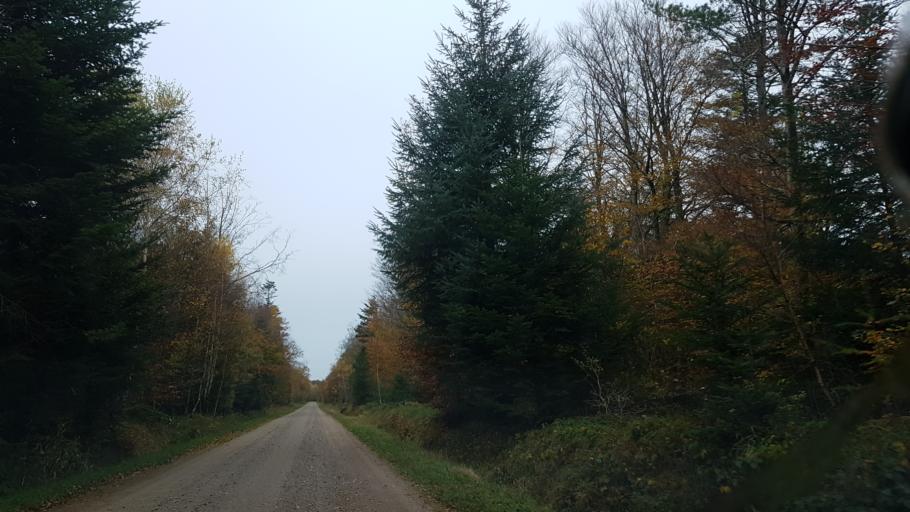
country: DK
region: South Denmark
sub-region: Tonder Kommune
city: Sherrebek
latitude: 55.1869
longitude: 8.7615
